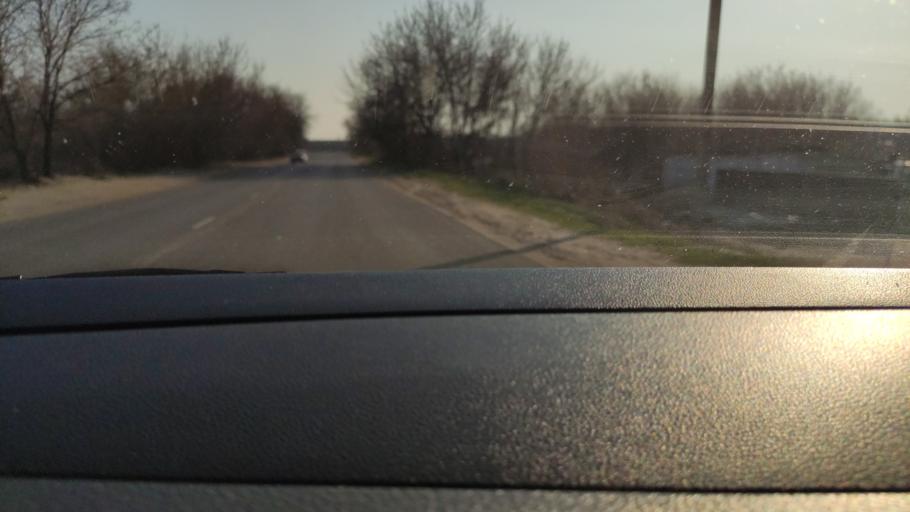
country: RU
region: Voronezj
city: Maslovka
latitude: 51.5796
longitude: 39.3147
